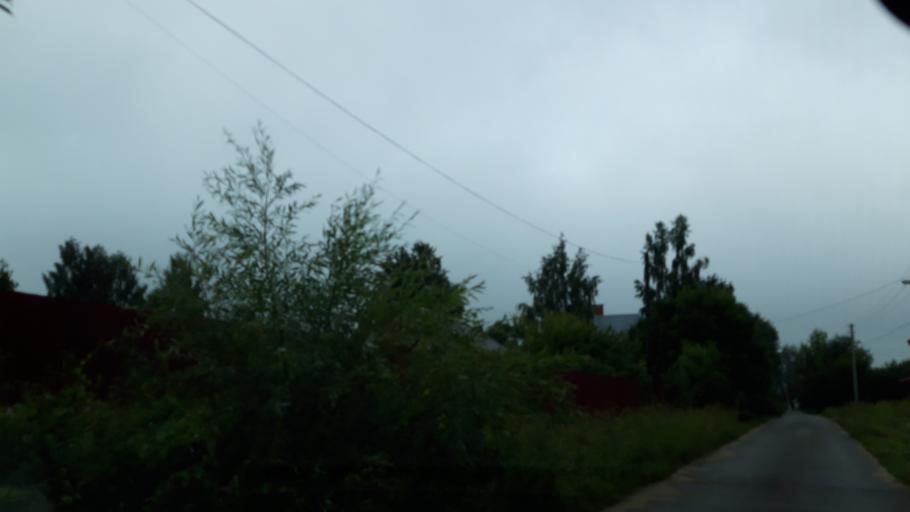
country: RU
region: Tverskaya
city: Konakovo
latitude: 56.6627
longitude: 36.6620
